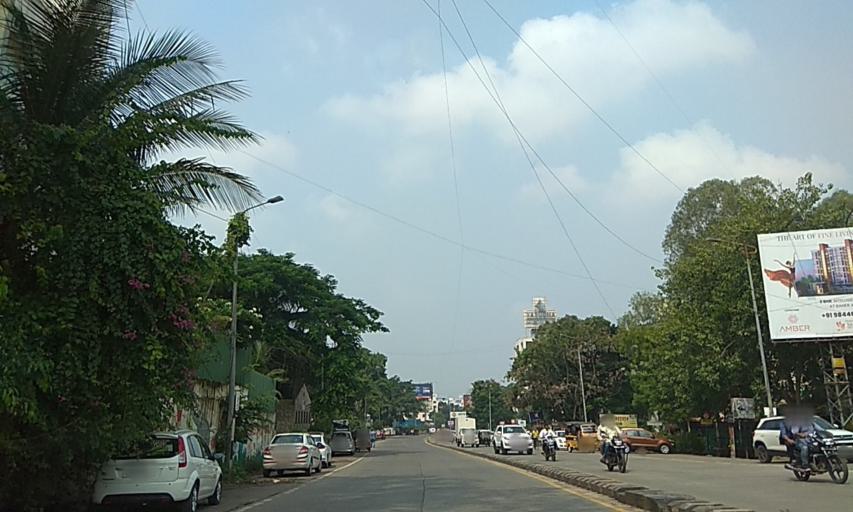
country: IN
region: Maharashtra
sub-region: Pune Division
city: Khadki
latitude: 18.5591
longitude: 73.7912
